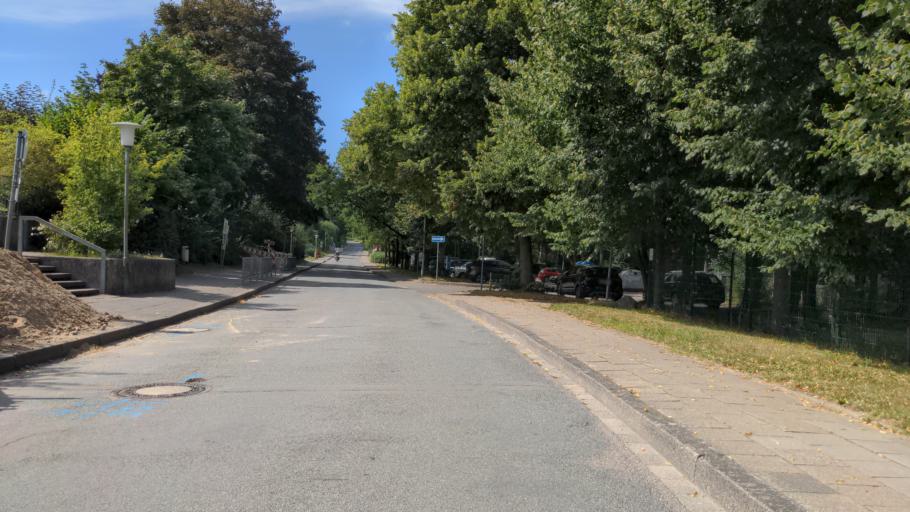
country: DE
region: Schleswig-Holstein
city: Malente
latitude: 54.1772
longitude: 10.5564
